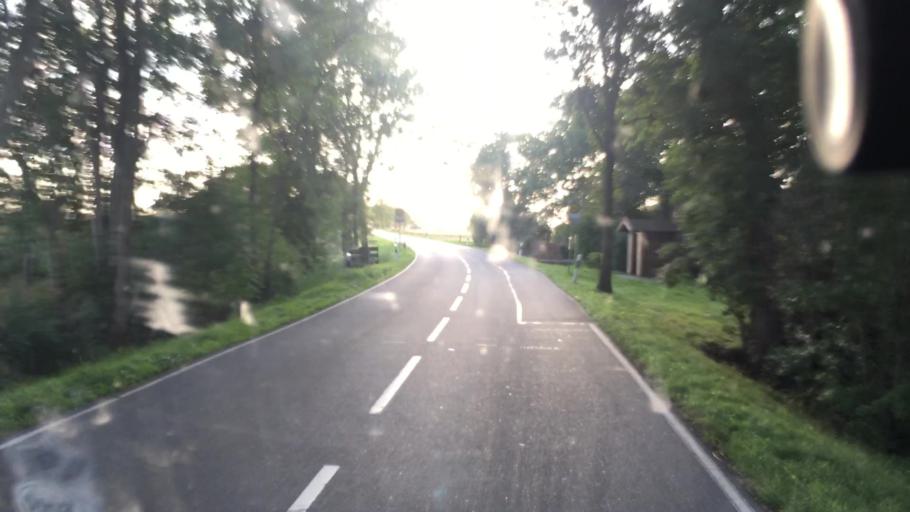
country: DE
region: Lower Saxony
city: Wittmund
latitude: 53.6432
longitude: 7.8086
